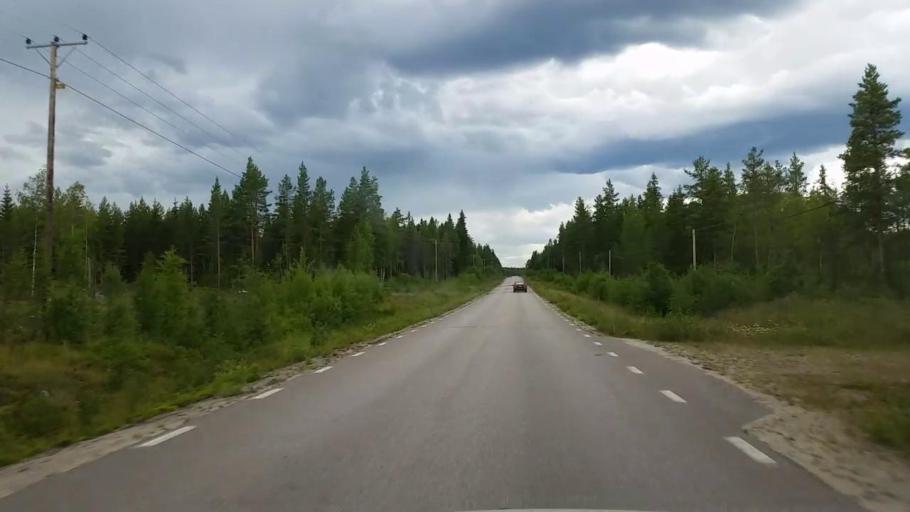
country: SE
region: Gaevleborg
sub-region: Ovanakers Kommun
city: Edsbyn
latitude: 61.4622
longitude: 15.8728
